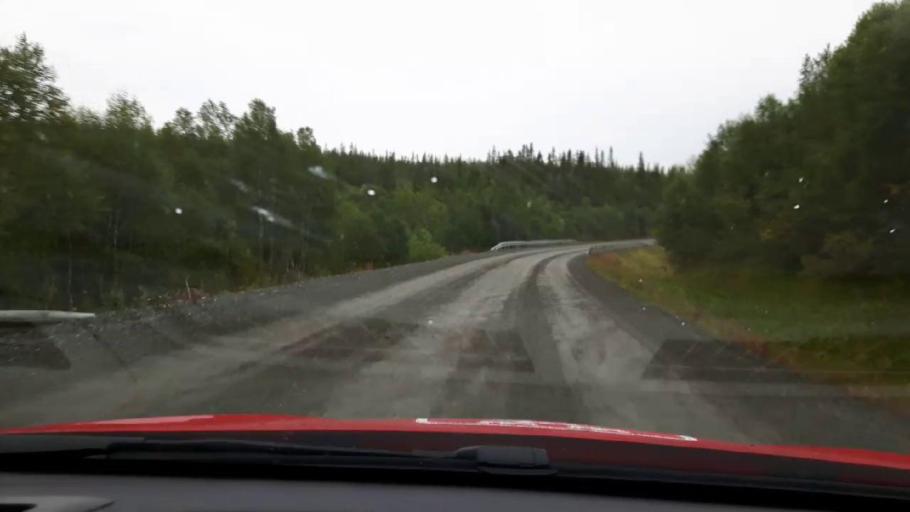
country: NO
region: Nord-Trondelag
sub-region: Meraker
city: Meraker
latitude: 63.5772
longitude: 12.2775
